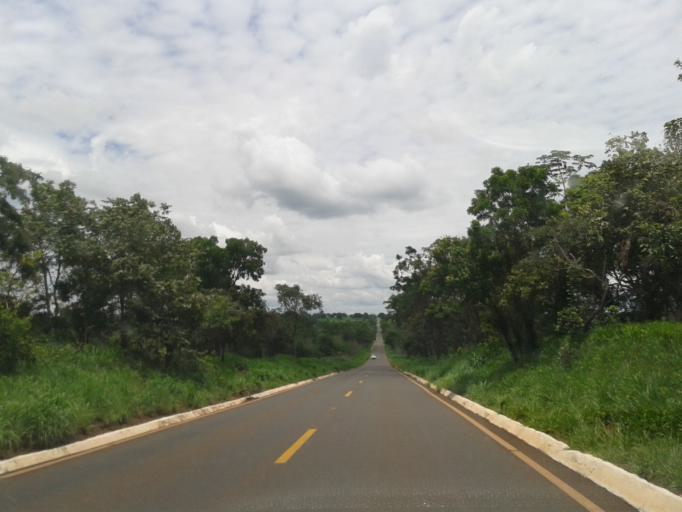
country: BR
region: Minas Gerais
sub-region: Santa Vitoria
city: Santa Vitoria
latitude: -18.9547
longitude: -49.8136
